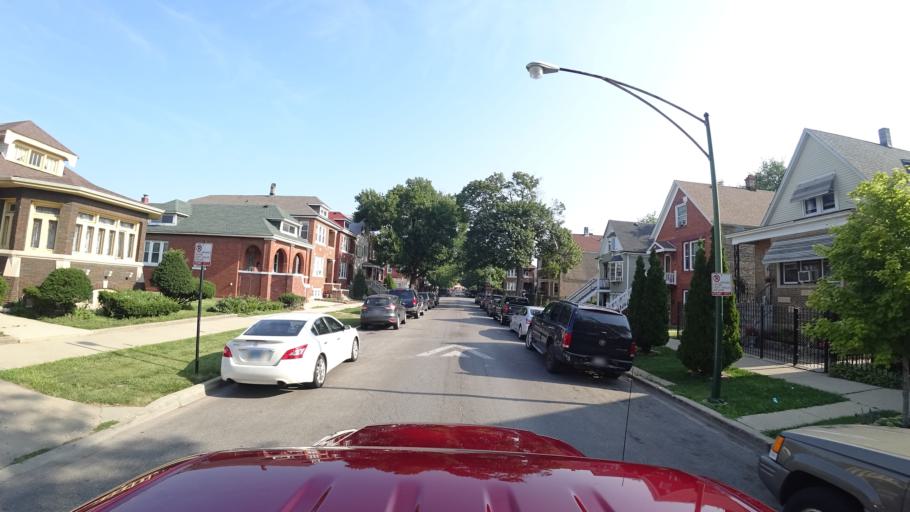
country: US
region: Illinois
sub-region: Cook County
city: Cicero
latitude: 41.8129
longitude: -87.7017
